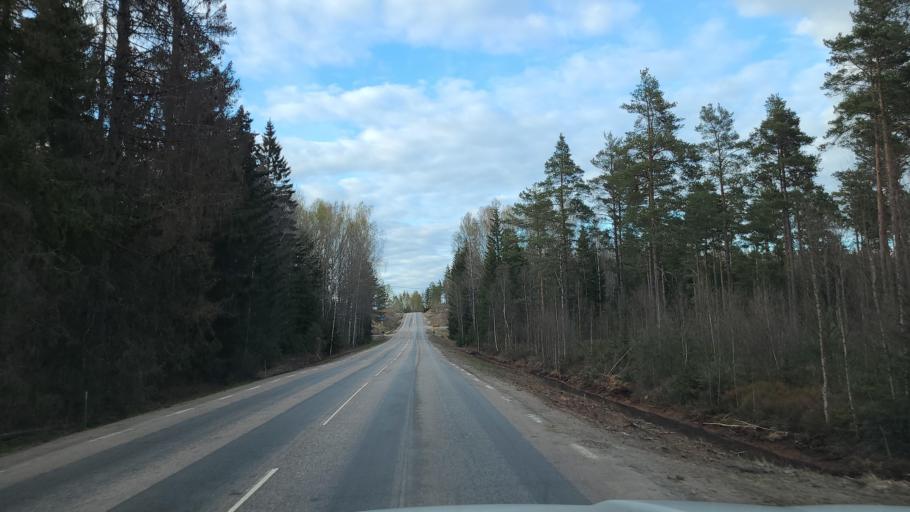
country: SE
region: Soedermanland
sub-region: Nykopings Kommun
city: Olstorp
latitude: 58.6994
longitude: 16.6382
